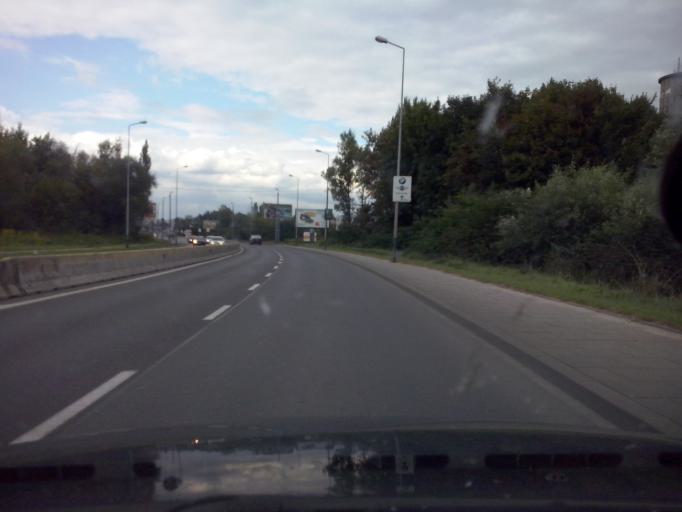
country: PL
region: Lesser Poland Voivodeship
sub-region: Krakow
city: Krakow
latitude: 50.0580
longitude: 20.0026
